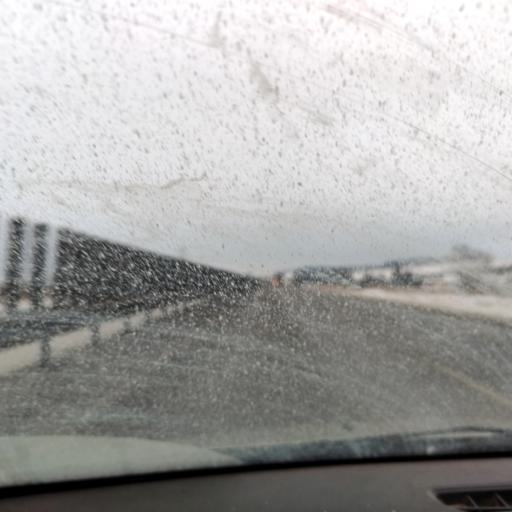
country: RU
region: Perm
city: Froly
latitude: 57.9358
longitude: 56.2505
